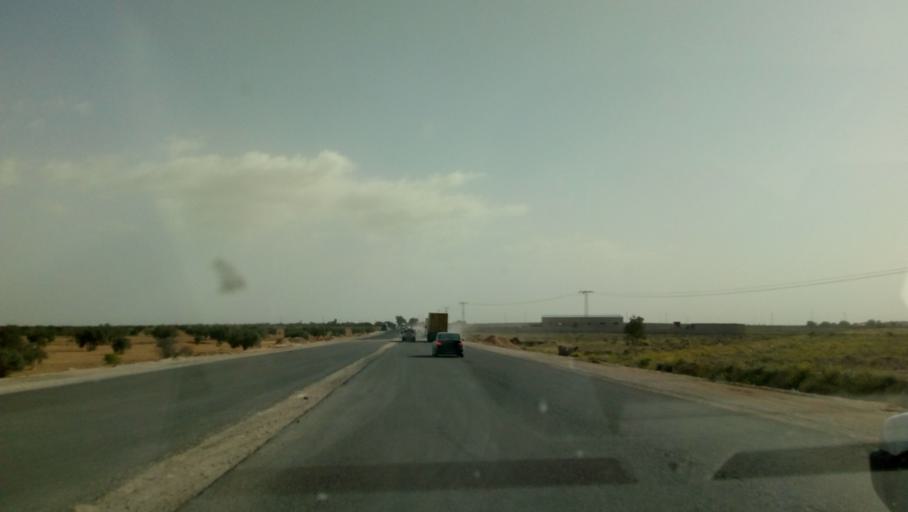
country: TN
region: Qabis
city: Gabes
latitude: 33.8826
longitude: 10.0087
